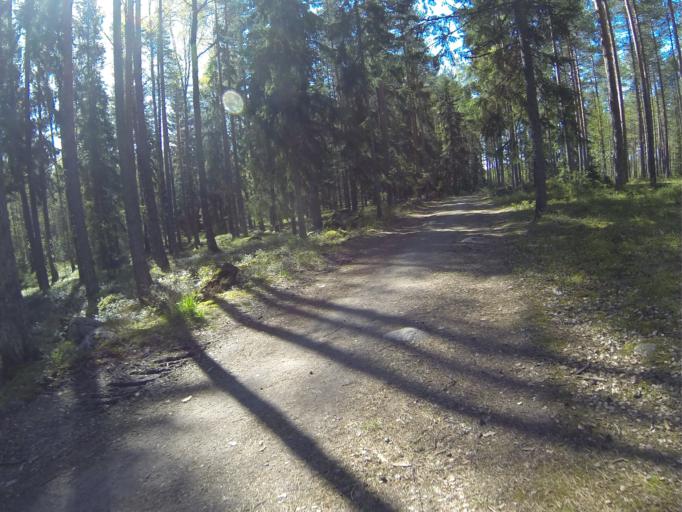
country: FI
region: Varsinais-Suomi
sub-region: Salo
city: Salo
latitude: 60.3966
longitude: 23.1976
